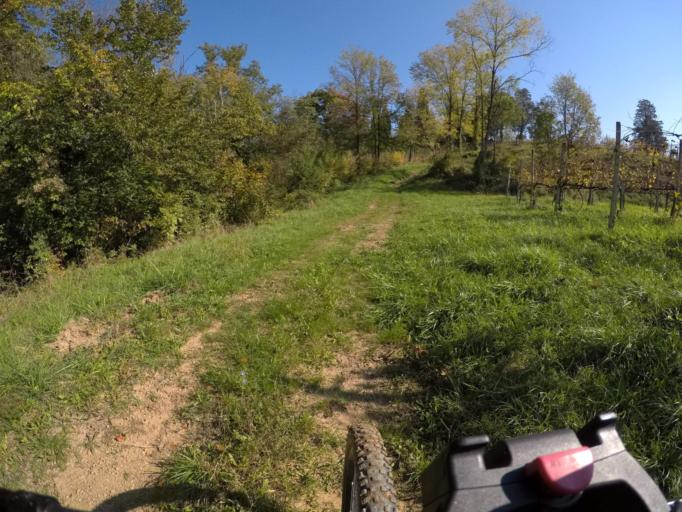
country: IT
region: Friuli Venezia Giulia
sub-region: Provincia di Udine
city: Manzano
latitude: 46.0072
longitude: 13.3751
